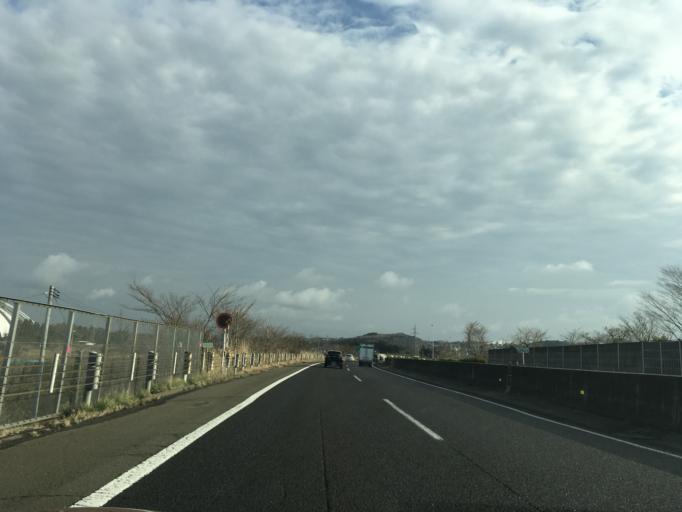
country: JP
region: Miyagi
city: Tomiya
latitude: 38.3337
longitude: 140.8559
